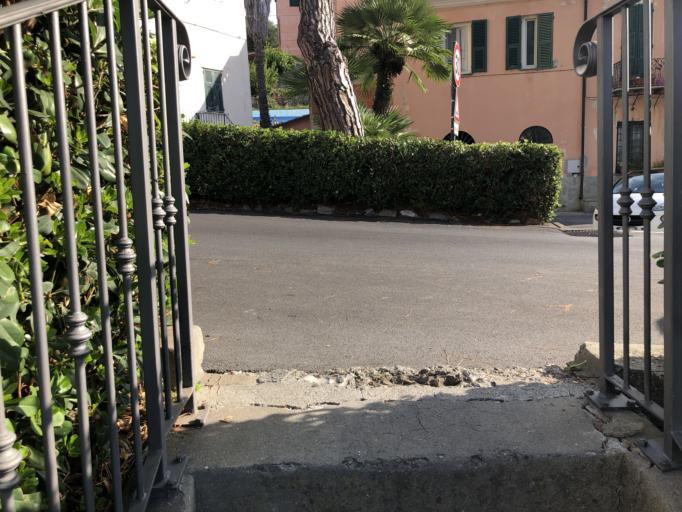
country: IT
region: Liguria
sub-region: Provincia di Imperia
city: Cipressa
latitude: 43.8517
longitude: 7.9305
